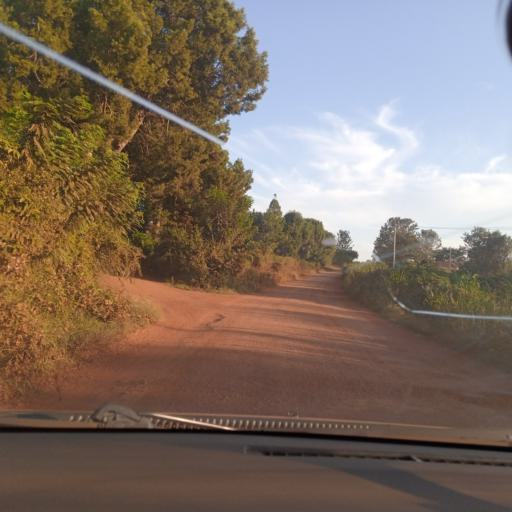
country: UG
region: Central Region
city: Masaka
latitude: -0.3391
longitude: 31.7626
